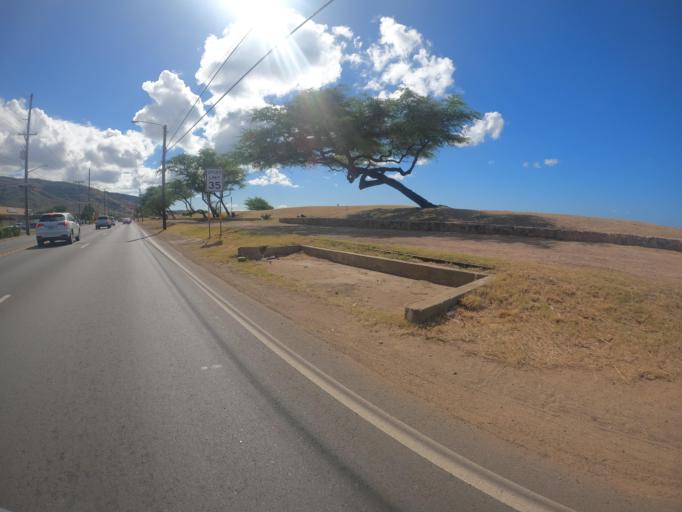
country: US
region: Hawaii
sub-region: Honolulu County
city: Nanakuli
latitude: 21.3864
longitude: -158.1523
